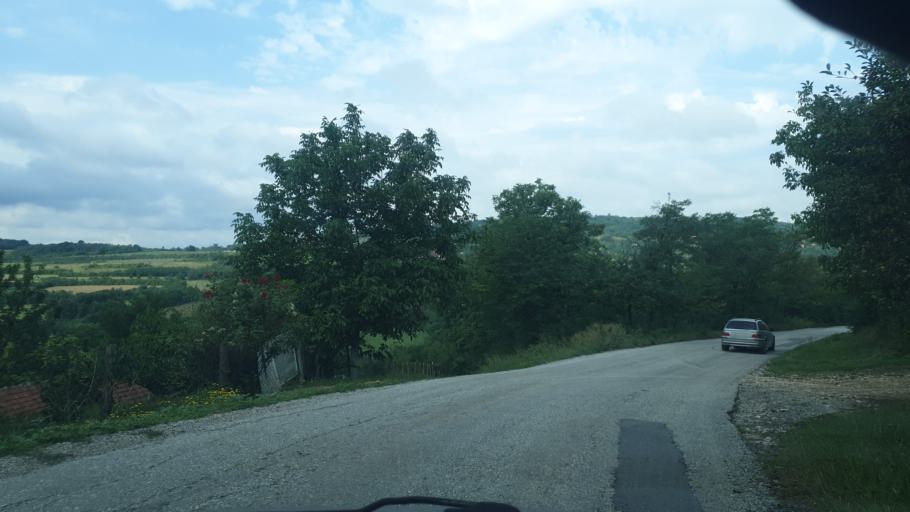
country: RS
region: Central Serbia
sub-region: Sumadijski Okrug
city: Kragujevac
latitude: 44.1030
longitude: 20.7930
